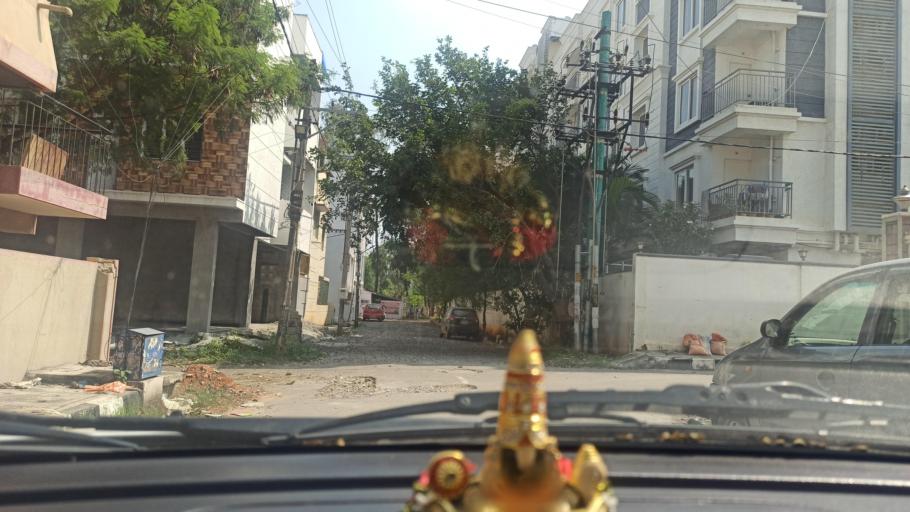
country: IN
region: Karnataka
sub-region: Bangalore Urban
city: Bangalore
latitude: 13.0214
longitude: 77.6612
